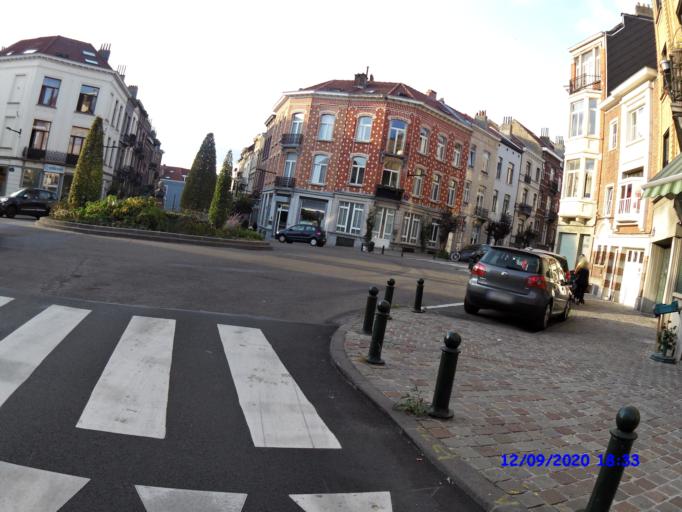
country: BE
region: Brussels Capital
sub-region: Bruxelles-Capitale
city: Brussels
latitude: 50.8274
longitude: 4.3773
